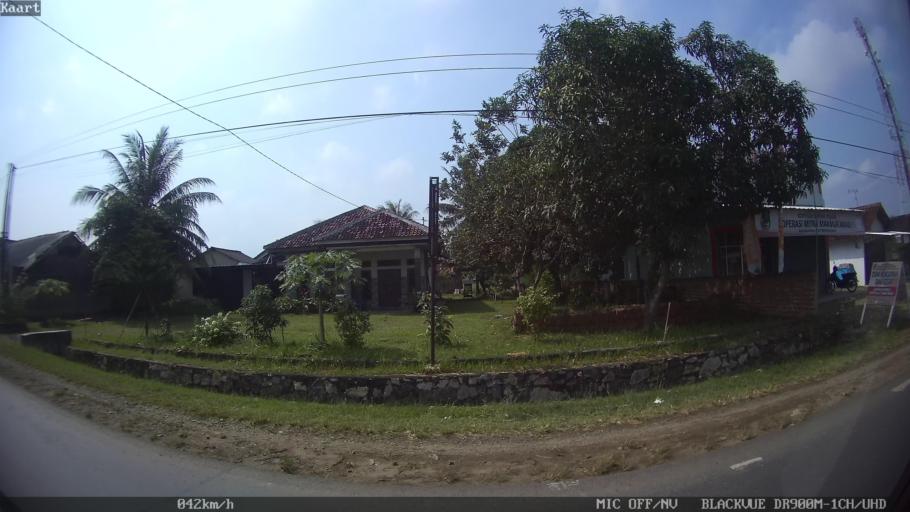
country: ID
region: Lampung
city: Gadingrejo
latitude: -5.3713
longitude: 105.0486
